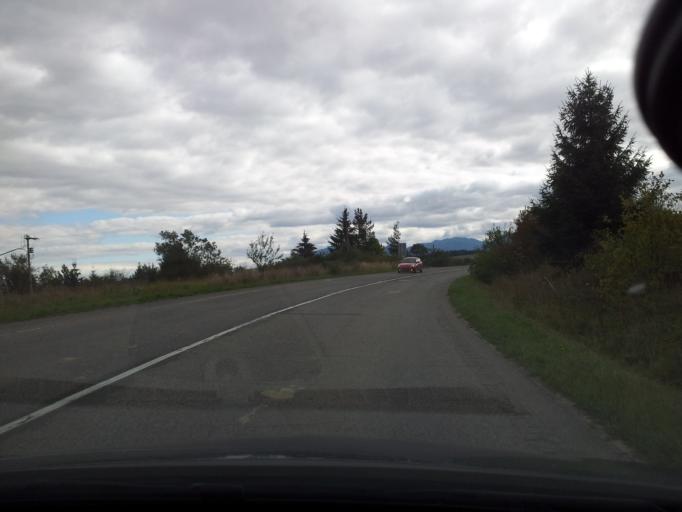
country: SK
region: Zilinsky
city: Ruzomberok
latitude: 49.0951
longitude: 19.4345
